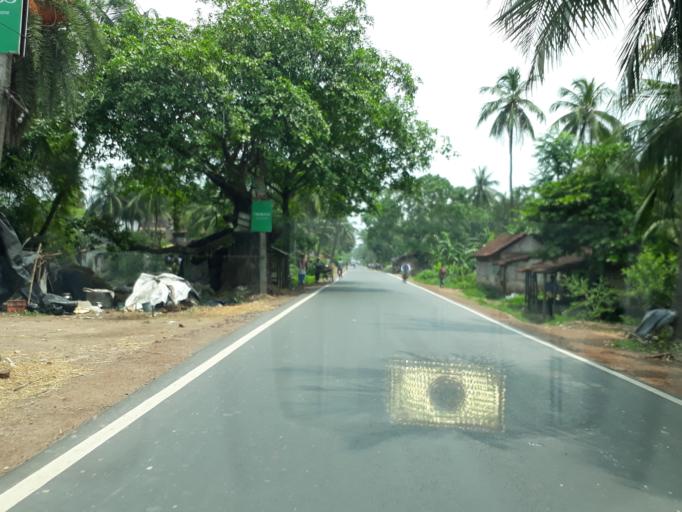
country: IN
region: West Bengal
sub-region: Purba Medinipur
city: Mahishadal
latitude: 22.1789
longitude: 87.9139
